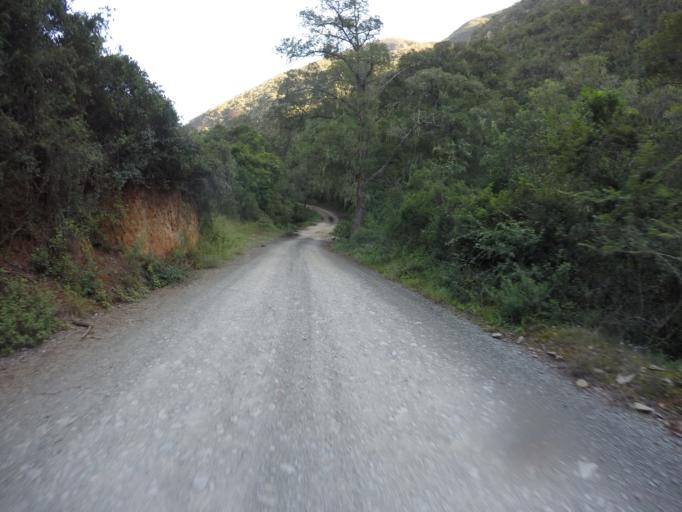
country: ZA
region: Eastern Cape
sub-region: Cacadu District Municipality
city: Kareedouw
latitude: -33.6535
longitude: 24.5222
